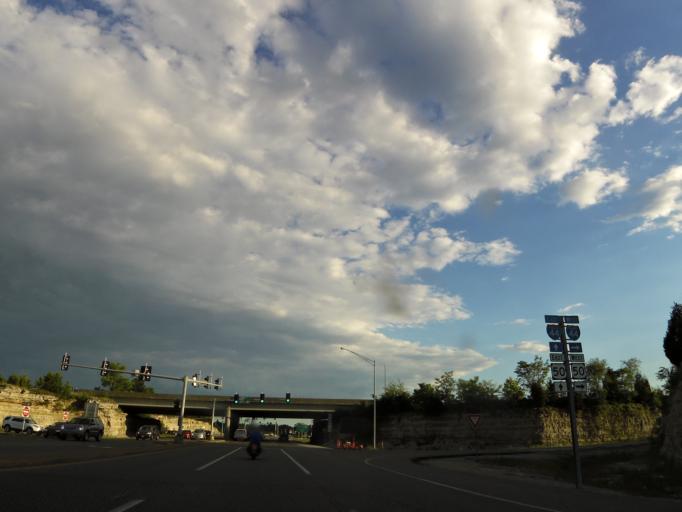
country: US
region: Missouri
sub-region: Saint Louis County
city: Eureka
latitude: 38.5074
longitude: -90.6233
